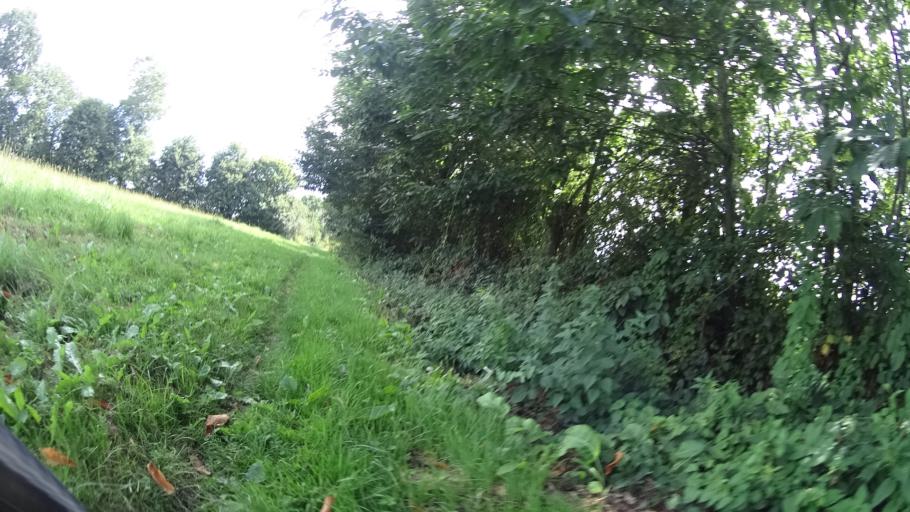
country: FR
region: Brittany
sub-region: Departement d'Ille-et-Vilaine
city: La Meziere
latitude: 48.2295
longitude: -1.7473
